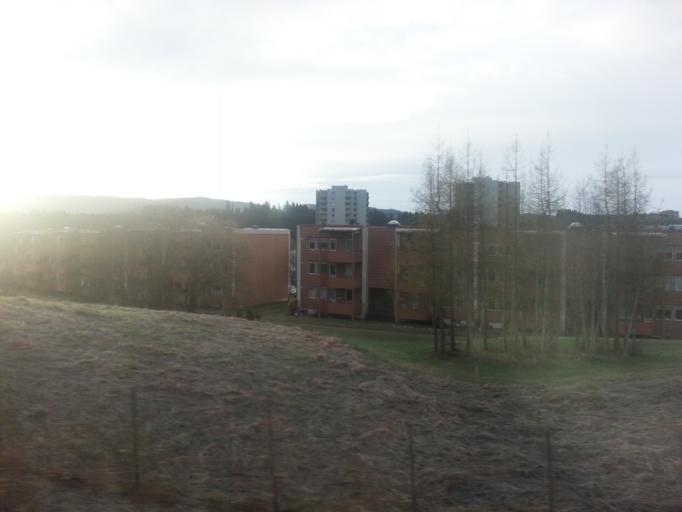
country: NO
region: Sor-Trondelag
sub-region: Trondheim
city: Trondheim
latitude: 63.3789
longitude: 10.3571
